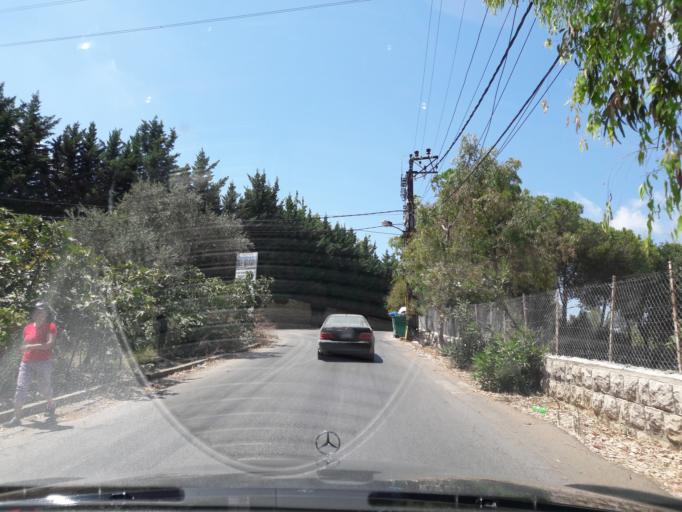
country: LB
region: Mont-Liban
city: Djounie
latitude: 33.9259
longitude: 35.6547
